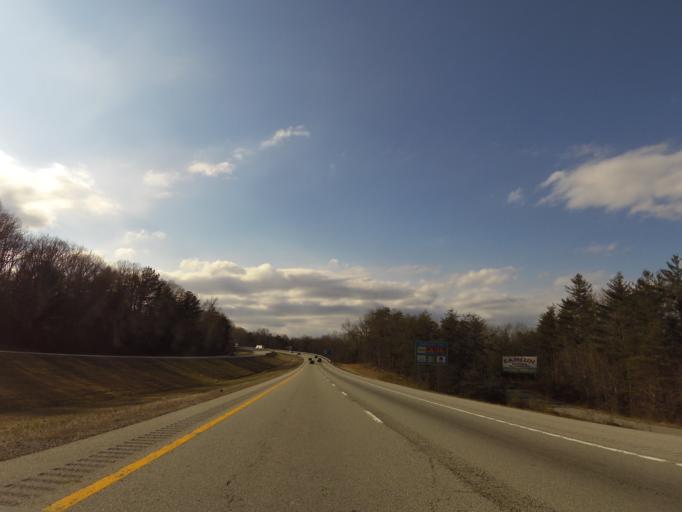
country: US
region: Tennessee
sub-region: Cumberland County
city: Crossville
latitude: 35.9565
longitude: -84.9570
